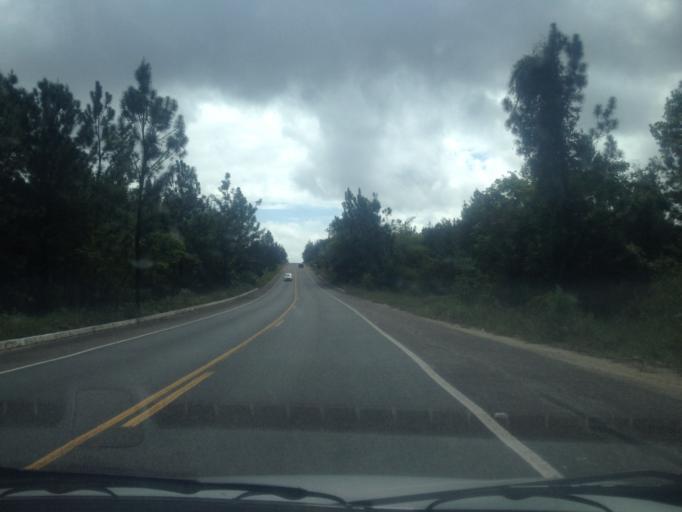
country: BR
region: Bahia
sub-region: Entre Rios
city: Entre Rios
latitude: -12.1390
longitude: -37.7914
